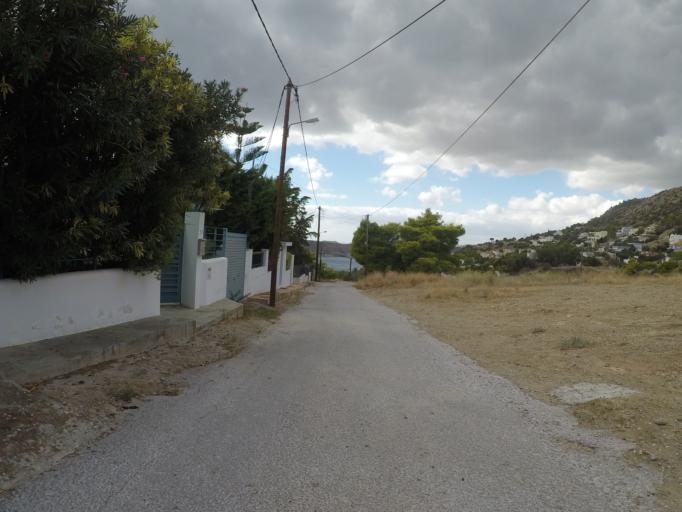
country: GR
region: Attica
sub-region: Nomarchia Anatolikis Attikis
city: Agios Dimitrios Kropias
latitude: 37.8059
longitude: 23.8561
